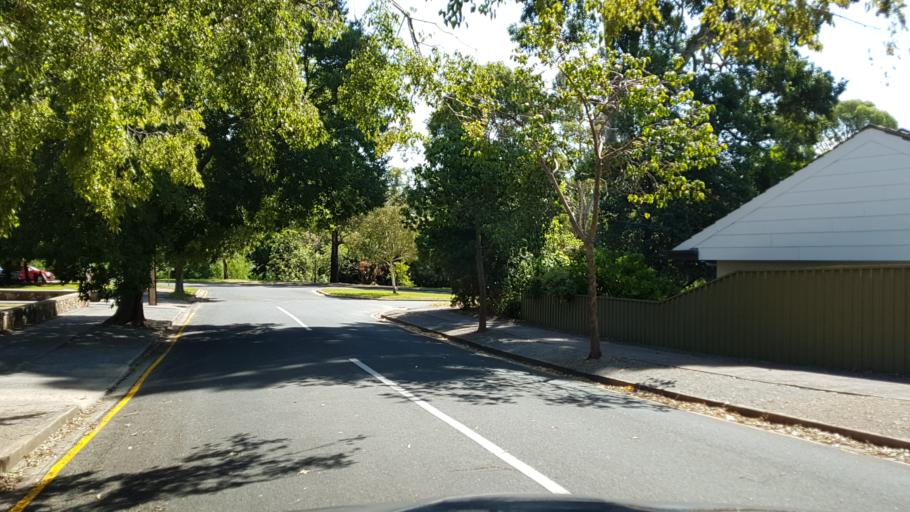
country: AU
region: South Australia
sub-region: Onkaparinga
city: Bedford Park
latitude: -35.0263
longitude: 138.5647
